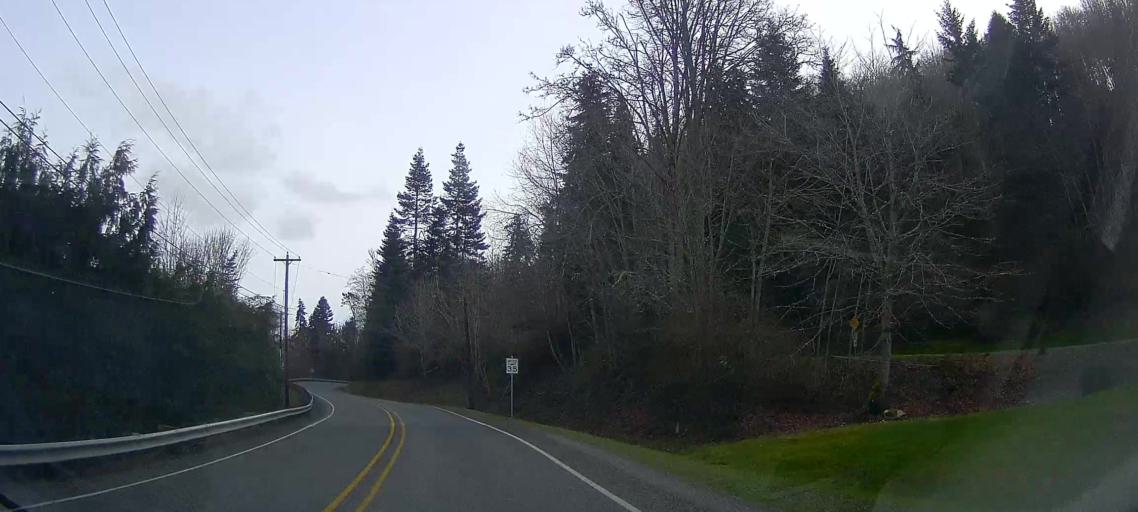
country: US
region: Washington
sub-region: Island County
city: Camano
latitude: 48.2529
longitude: -122.4998
